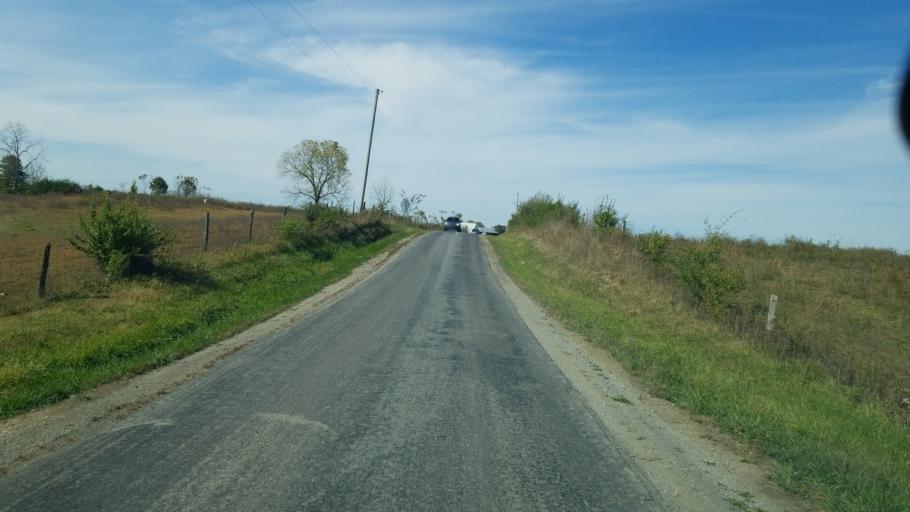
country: US
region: Ohio
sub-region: Highland County
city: Leesburg
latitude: 39.2875
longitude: -83.4831
